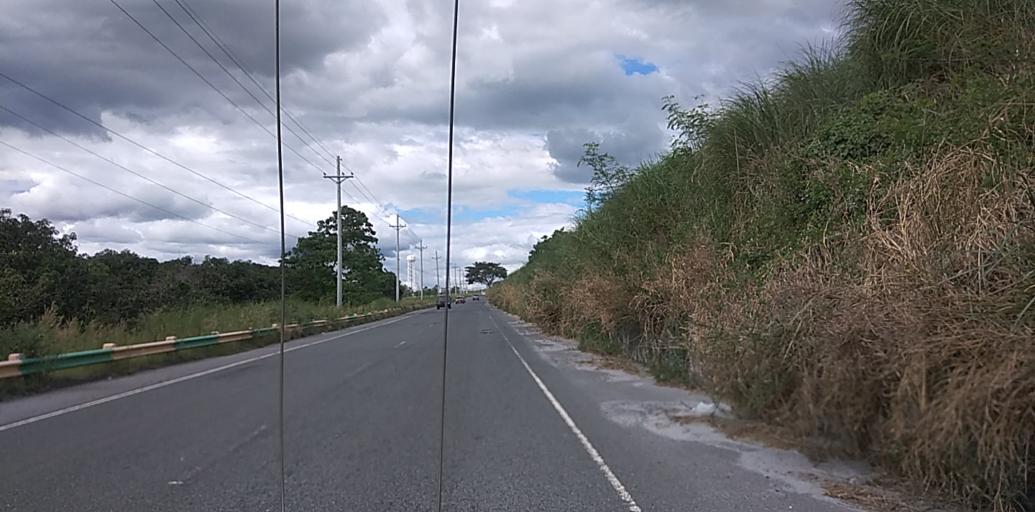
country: PH
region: Central Luzon
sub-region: Province of Pampanga
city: Dolores
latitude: 15.1063
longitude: 120.5205
